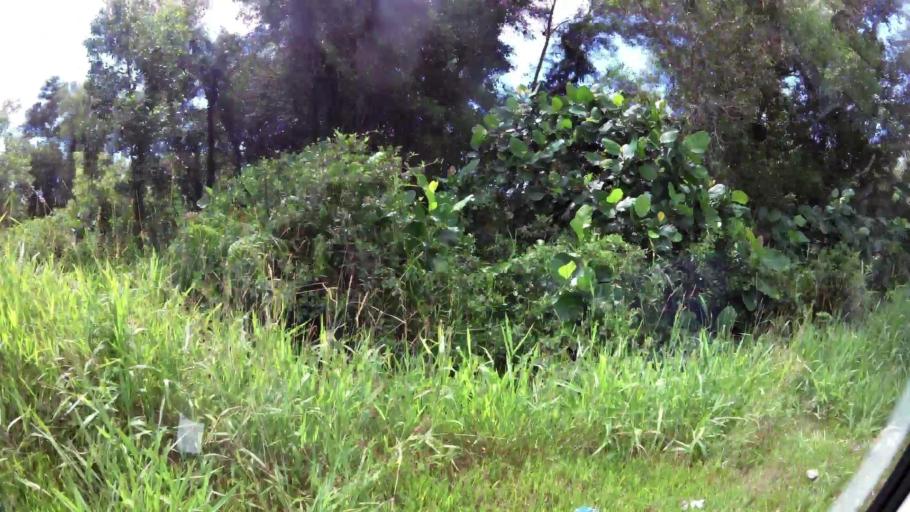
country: BN
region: Brunei and Muara
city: Bandar Seri Begawan
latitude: 4.9940
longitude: 114.9456
